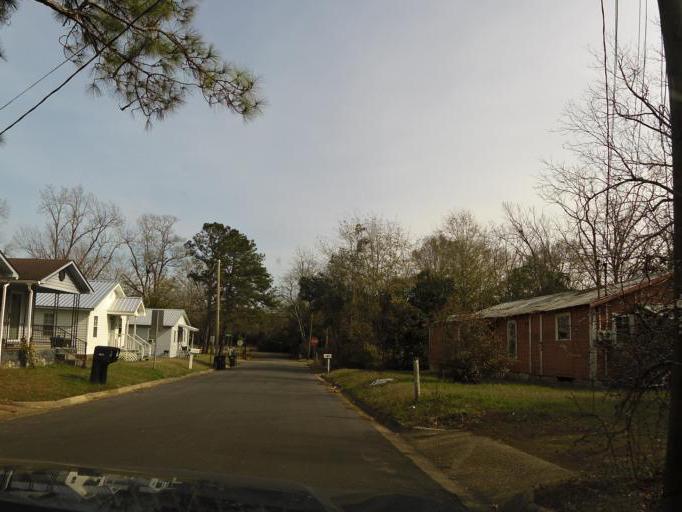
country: US
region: Alabama
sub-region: Houston County
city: Dothan
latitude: 31.2262
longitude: -85.3752
